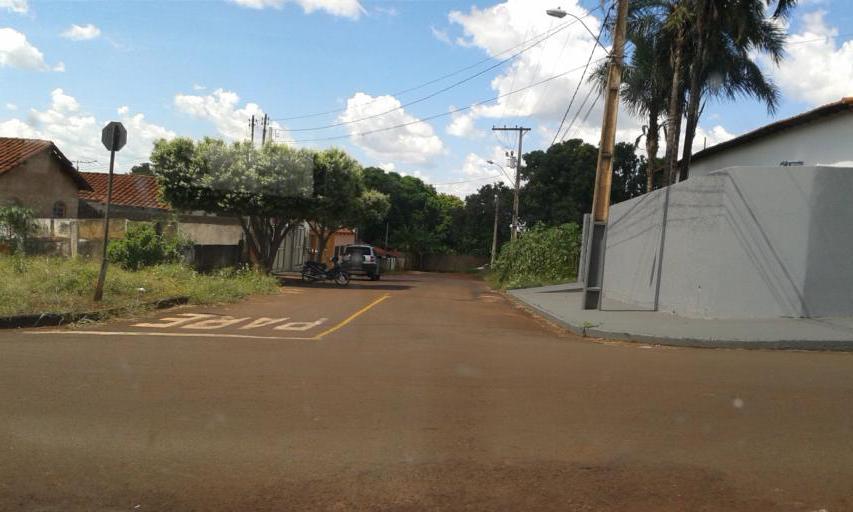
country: BR
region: Minas Gerais
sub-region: Ituiutaba
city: Ituiutaba
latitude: -18.9691
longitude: -49.4770
